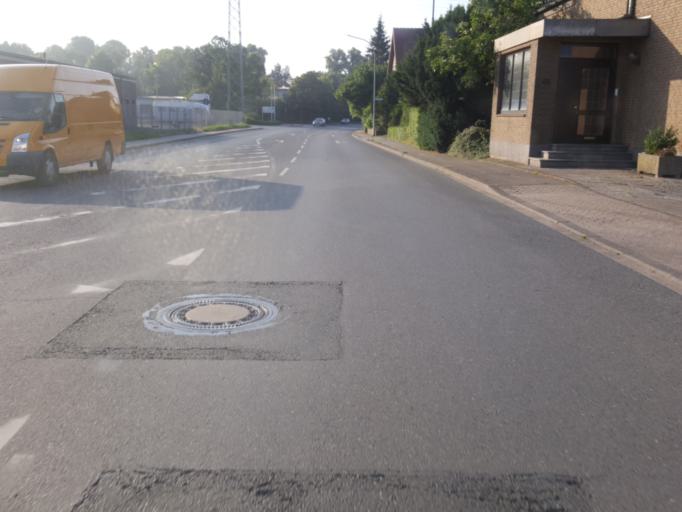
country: DE
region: North Rhine-Westphalia
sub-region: Regierungsbezirk Detmold
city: Kirchlengern
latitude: 52.1899
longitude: 8.6484
